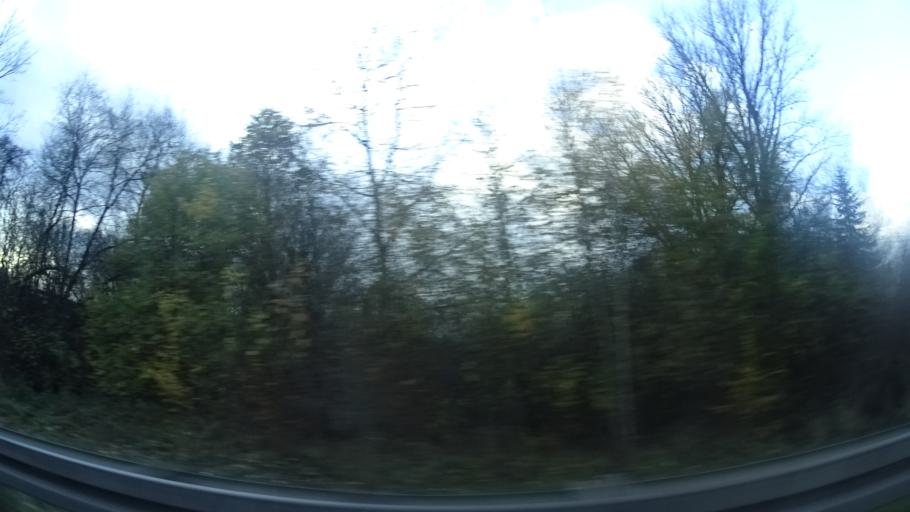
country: DE
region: Hesse
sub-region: Regierungsbezirk Kassel
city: Kunzell
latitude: 50.5327
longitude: 9.6956
